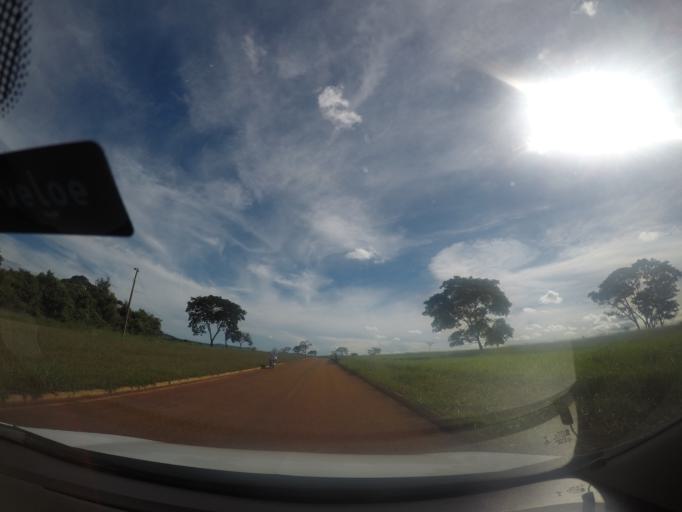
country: BR
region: Goias
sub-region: Inhumas
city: Inhumas
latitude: -16.4069
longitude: -49.4710
